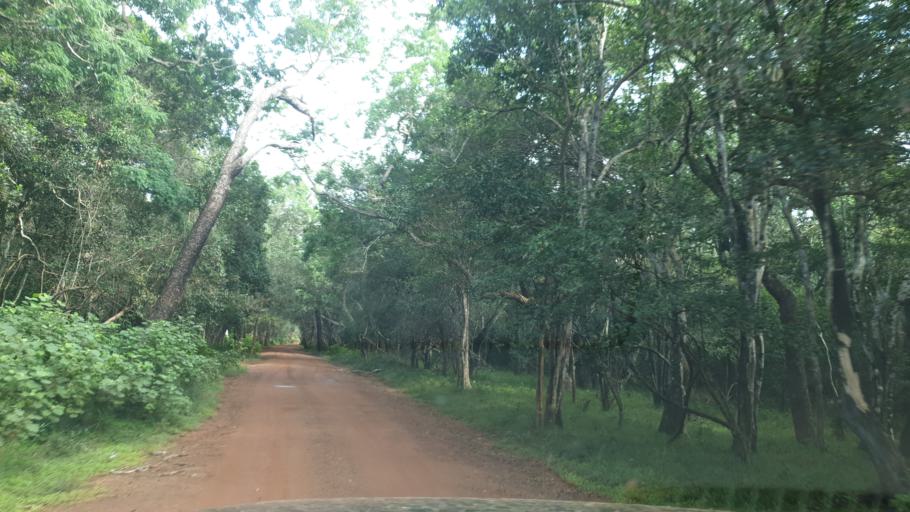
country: LK
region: North Central
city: Anuradhapura
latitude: 8.3799
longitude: 80.0663
